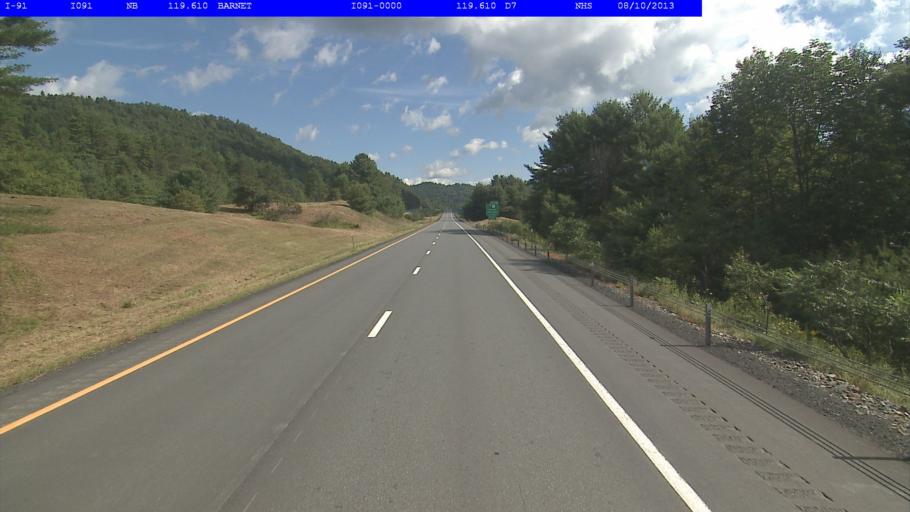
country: US
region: New Hampshire
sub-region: Grafton County
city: Woodsville
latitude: 44.2876
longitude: -72.0641
